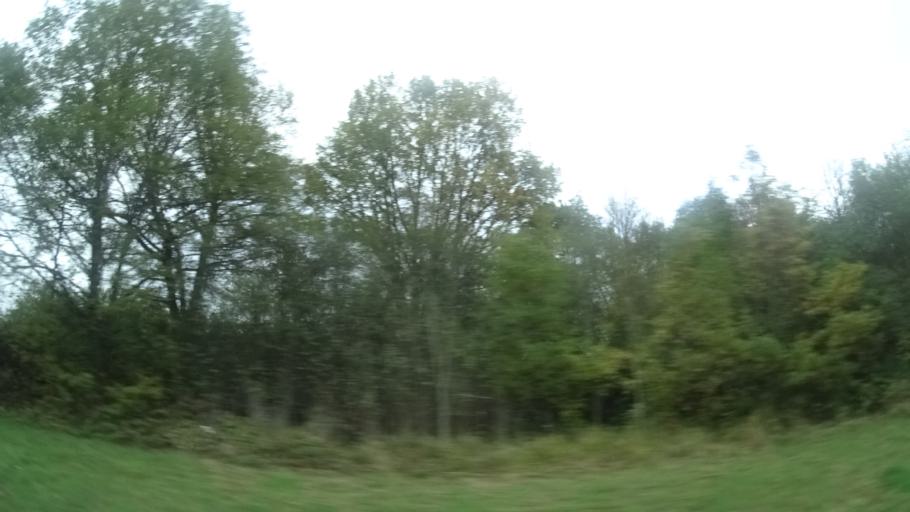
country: DE
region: Bavaria
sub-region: Regierungsbezirk Unterfranken
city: Oberelsbach
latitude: 50.4010
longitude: 10.0786
